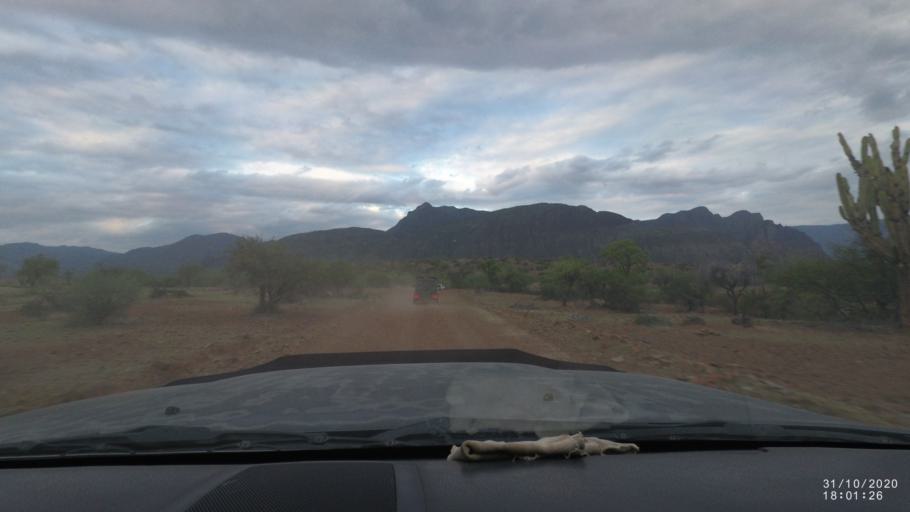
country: BO
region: Chuquisaca
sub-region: Provincia Zudanez
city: Mojocoya
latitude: -18.6641
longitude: -64.5310
